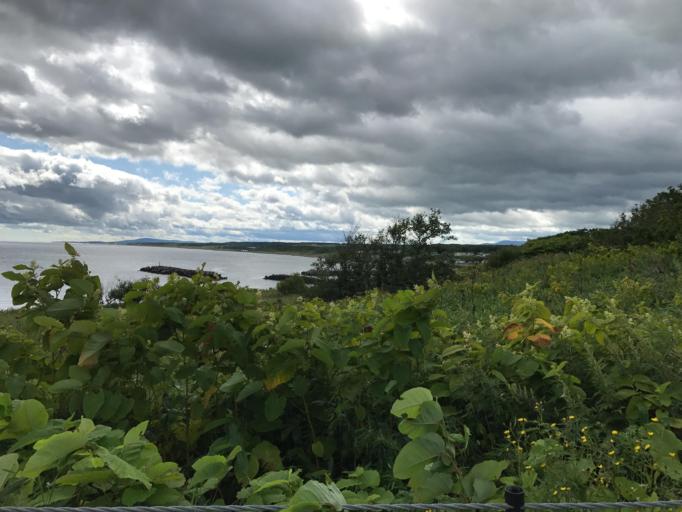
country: JP
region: Hokkaido
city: Mombetsu
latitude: 44.5268
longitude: 143.0605
